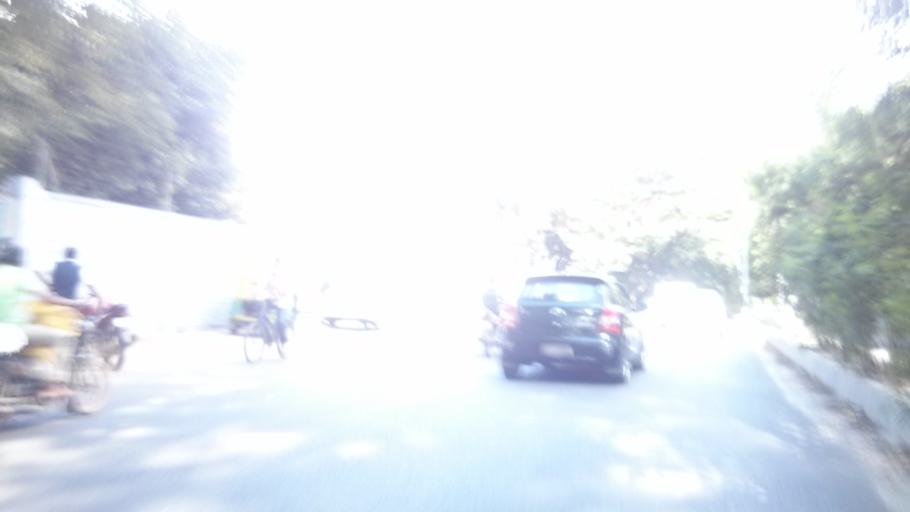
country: IN
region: Karnataka
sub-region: Bangalore Urban
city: Bangalore
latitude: 12.9557
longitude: 77.6773
